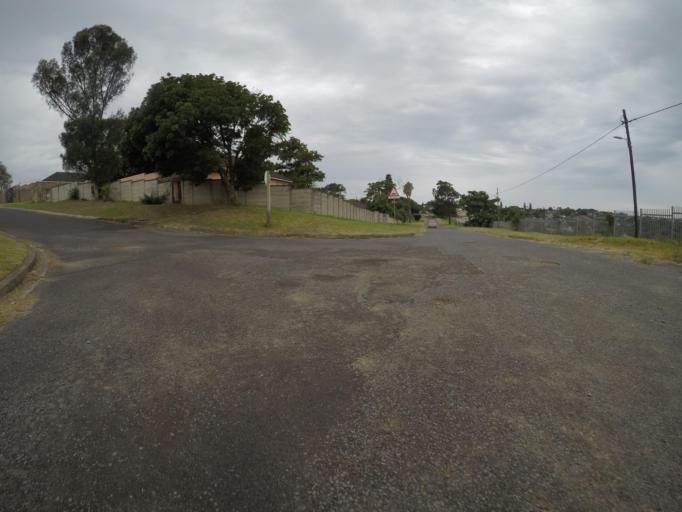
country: ZA
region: Eastern Cape
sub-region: Buffalo City Metropolitan Municipality
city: East London
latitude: -32.9896
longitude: 27.8564
